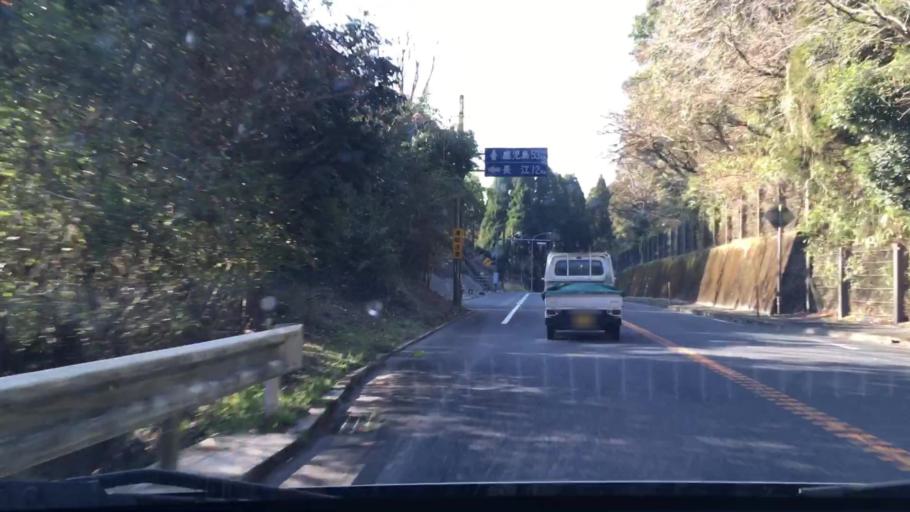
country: JP
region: Kagoshima
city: Sueyoshicho-ninokata
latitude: 31.6638
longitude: 130.9041
